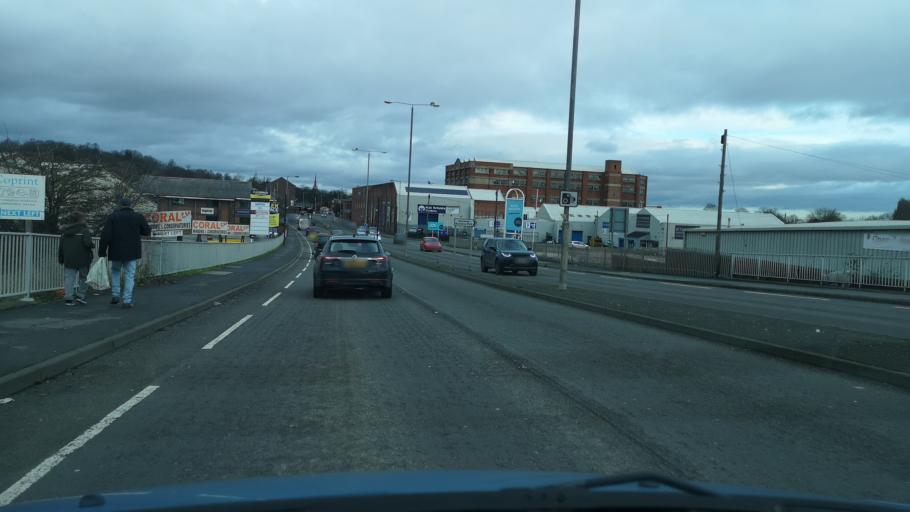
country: GB
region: England
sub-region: City and Borough of Wakefield
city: Wakefield
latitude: 53.6653
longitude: -1.5070
